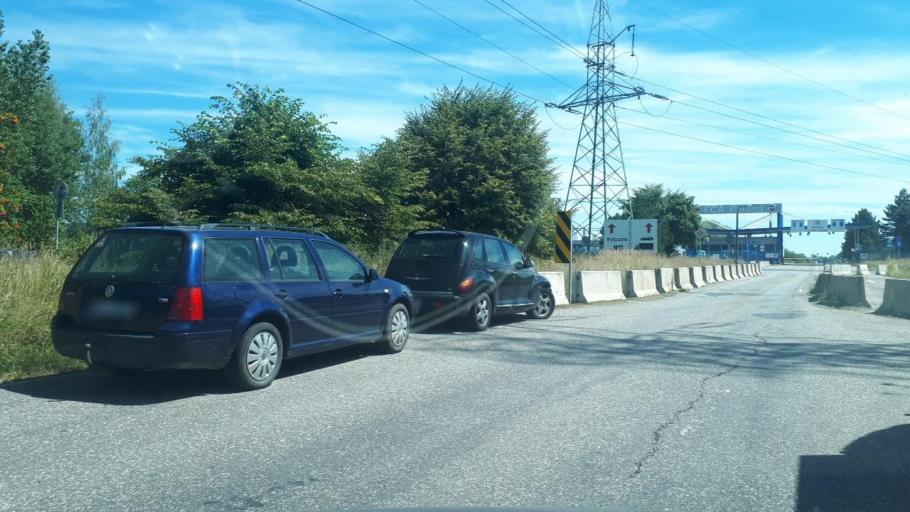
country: PL
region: Silesian Voivodeship
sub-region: Powiat bierunsko-ledzinski
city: Bierun
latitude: 50.1059
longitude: 19.0597
